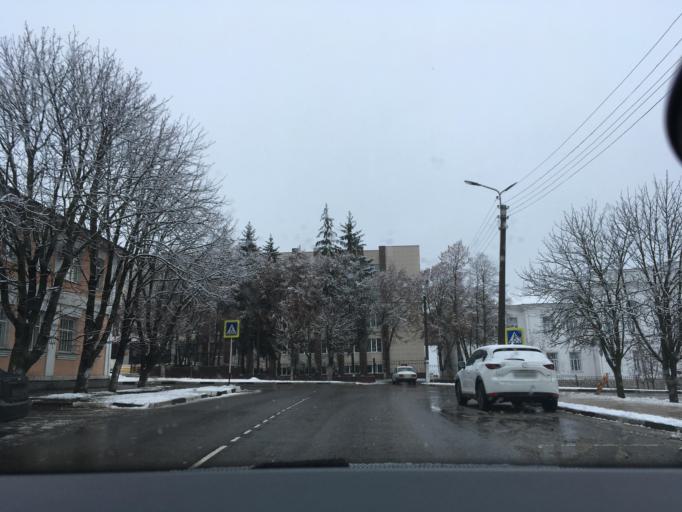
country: RU
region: Belgorod
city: Valuyki
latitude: 50.2124
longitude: 38.1023
